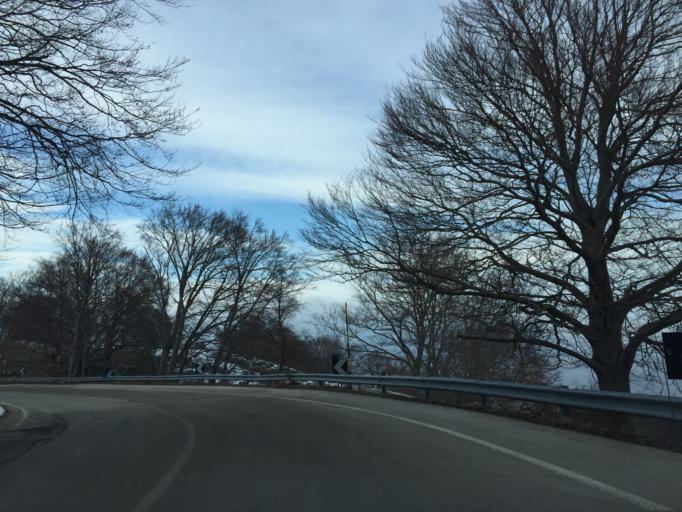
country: IT
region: Molise
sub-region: Provincia di Campobasso
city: San Massimo
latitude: 41.4676
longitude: 14.4175
